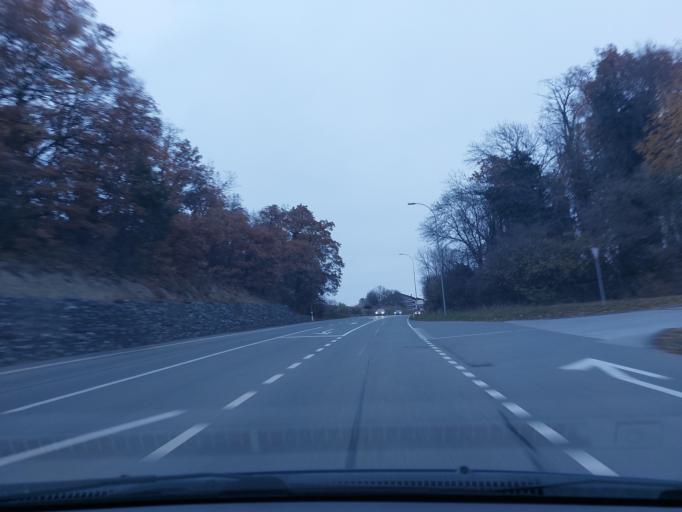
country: CH
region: Valais
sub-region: Sion District
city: Saviese
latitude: 46.2427
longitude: 7.3398
